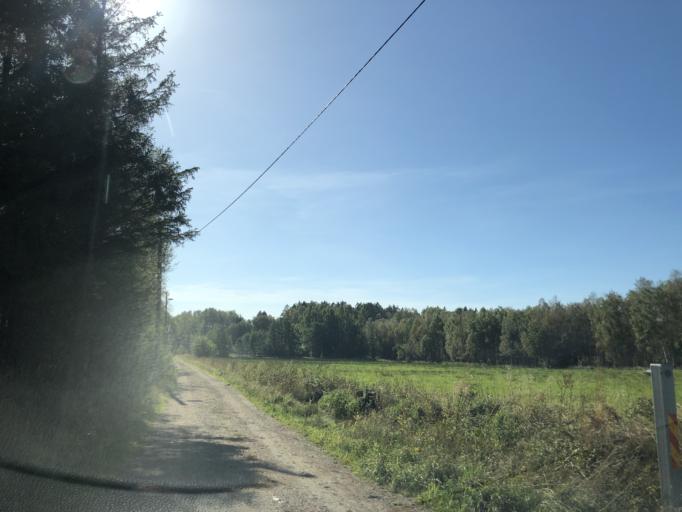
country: SE
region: Vaestra Goetaland
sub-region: Goteborg
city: Majorna
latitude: 57.7647
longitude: 11.9119
